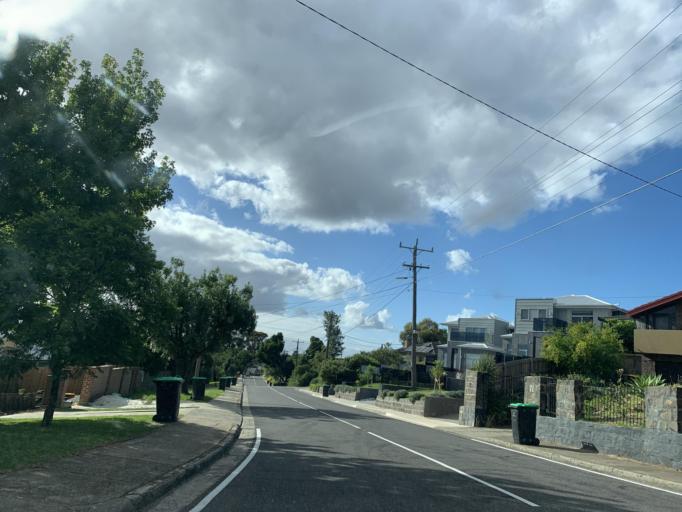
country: AU
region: Victoria
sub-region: Moreland
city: Oak Park
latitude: -37.7259
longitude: 144.9135
